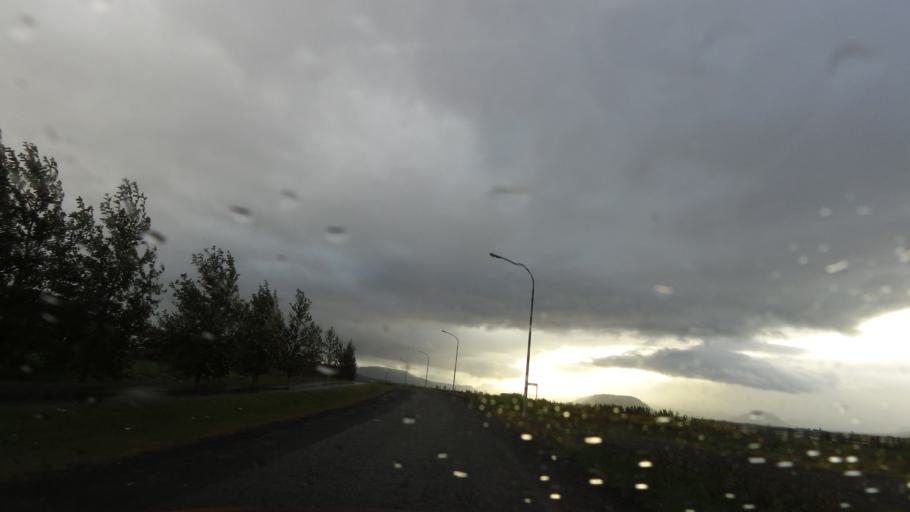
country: IS
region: West
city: Borgarnes
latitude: 64.3806
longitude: -21.8420
